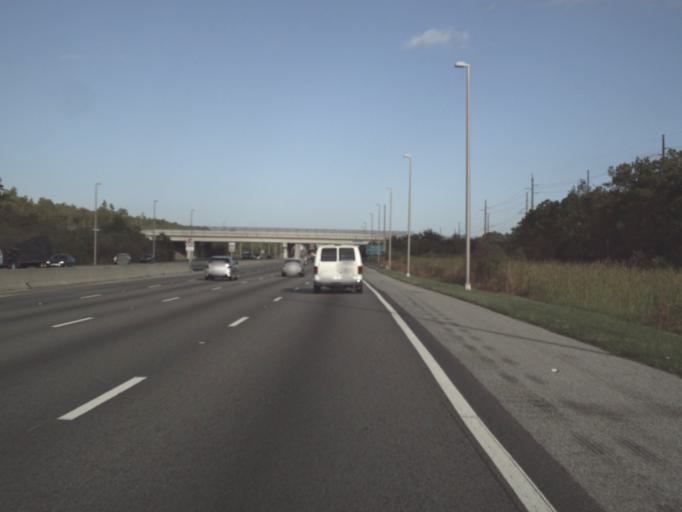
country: US
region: Florida
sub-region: Orange County
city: Oak Ridge
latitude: 28.4544
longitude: -81.4243
